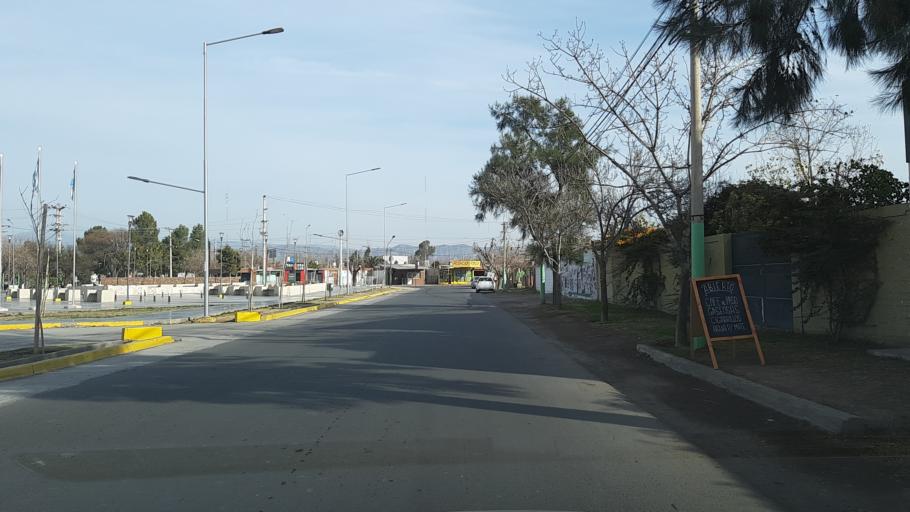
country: AR
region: San Juan
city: San Juan
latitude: -31.5319
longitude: -68.5929
